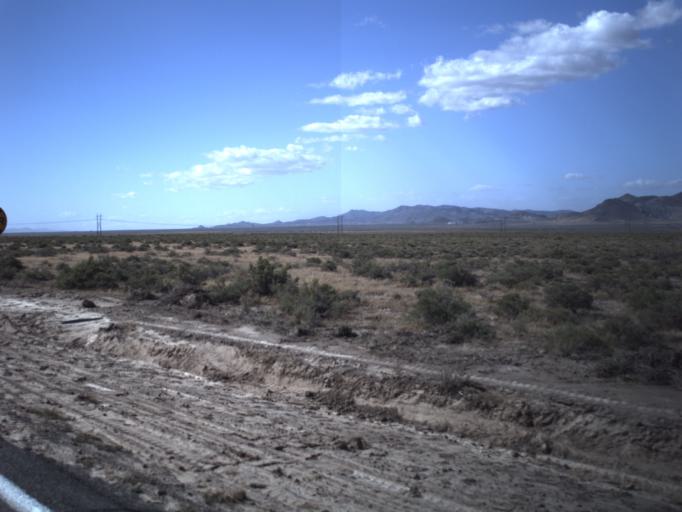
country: US
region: Utah
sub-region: Beaver County
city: Milford
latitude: 38.4977
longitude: -112.9912
